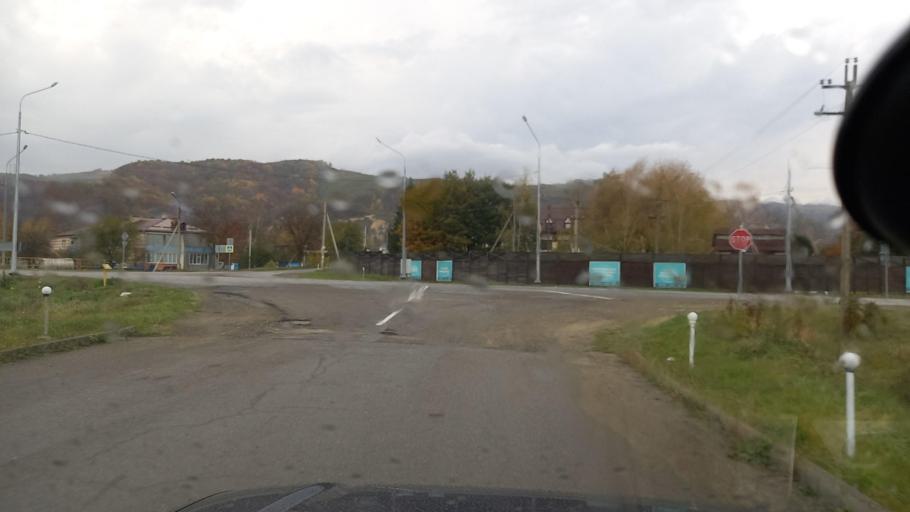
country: RU
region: Krasnodarskiy
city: Shedok
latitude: 44.1722
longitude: 40.8414
